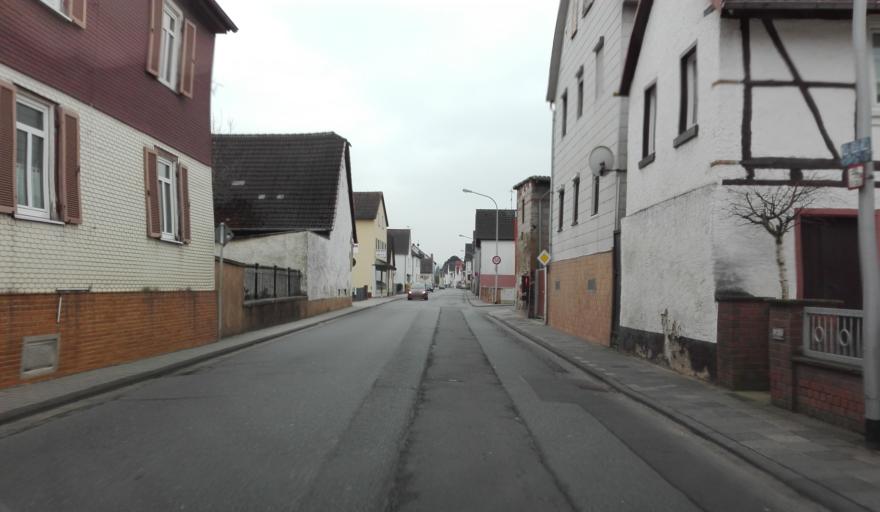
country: DE
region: Hesse
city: Ober-Ramstadt
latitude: 49.8009
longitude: 8.7378
